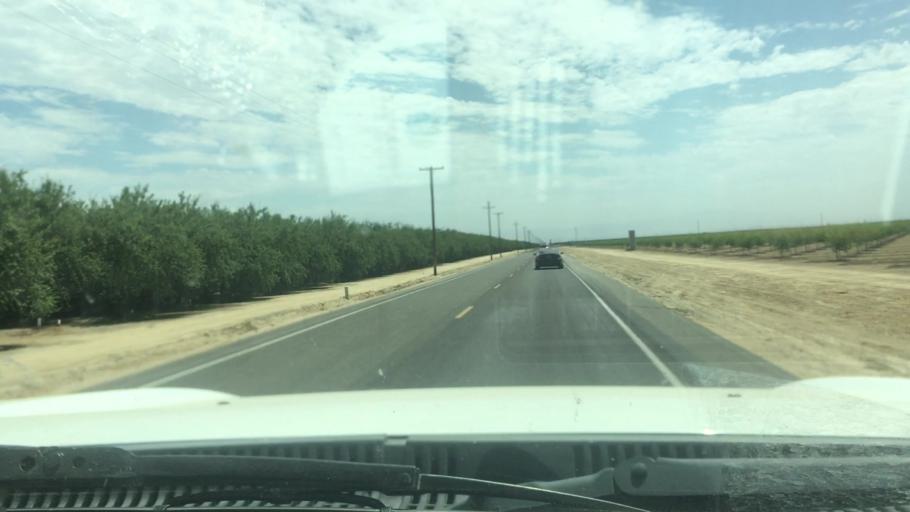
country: US
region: California
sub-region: Kern County
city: Wasco
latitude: 35.5580
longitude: -119.3103
